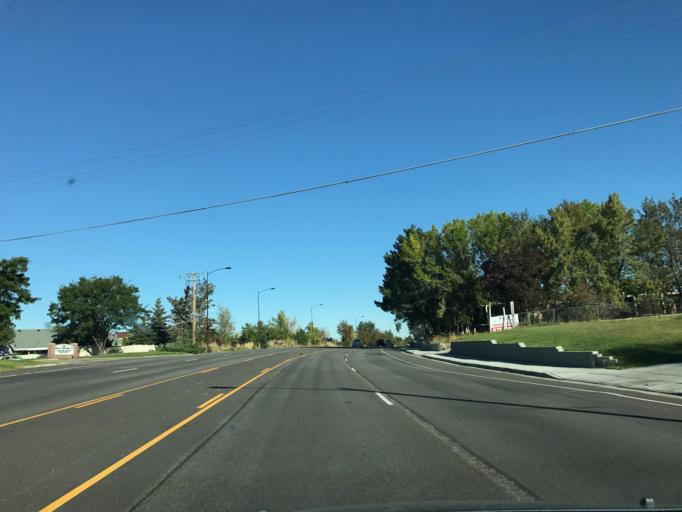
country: US
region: Utah
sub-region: Weber County
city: Washington Terrace
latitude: 41.1722
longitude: -111.9483
